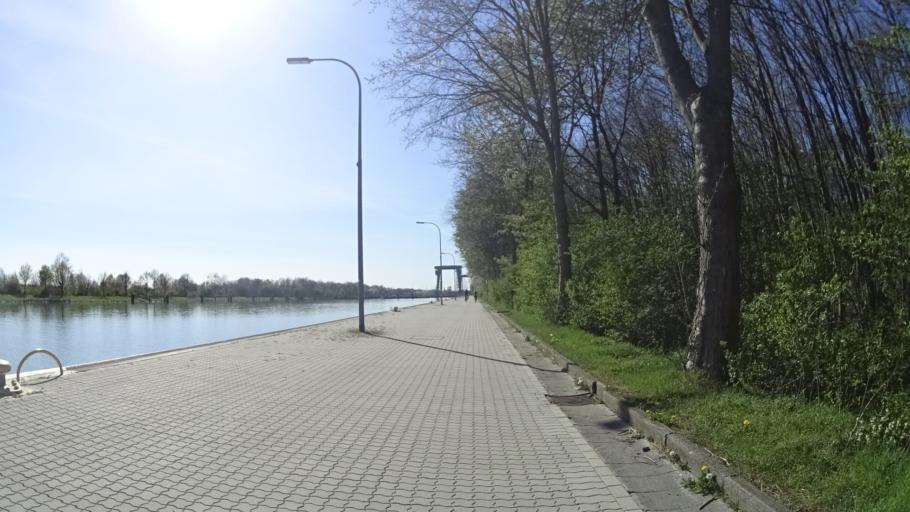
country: DE
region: North Rhine-Westphalia
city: Dorsten
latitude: 51.6632
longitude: 7.0139
